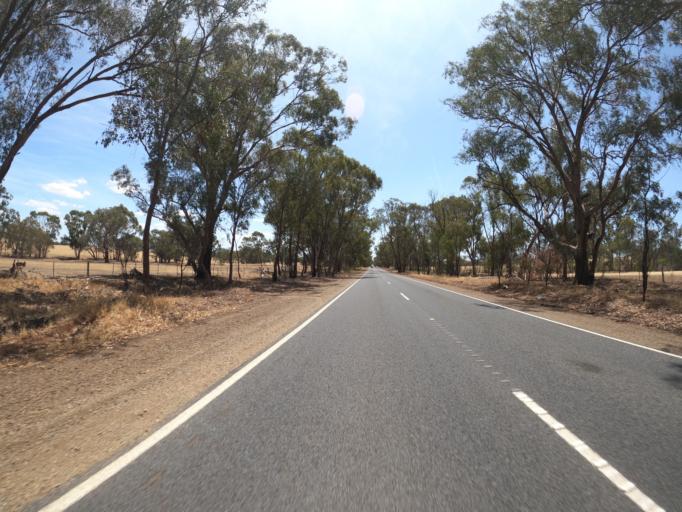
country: AU
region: Victoria
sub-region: Benalla
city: Benalla
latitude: -36.3664
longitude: 145.9703
